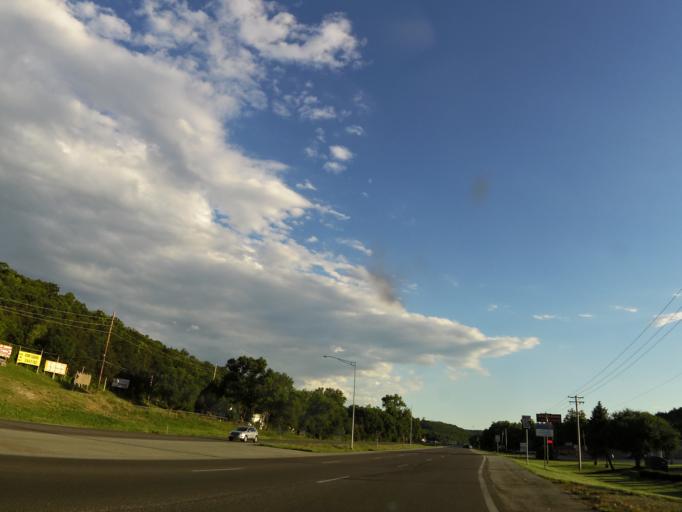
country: US
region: Missouri
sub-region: Jefferson County
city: Byrnes Mill
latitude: 38.4128
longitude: -90.5827
